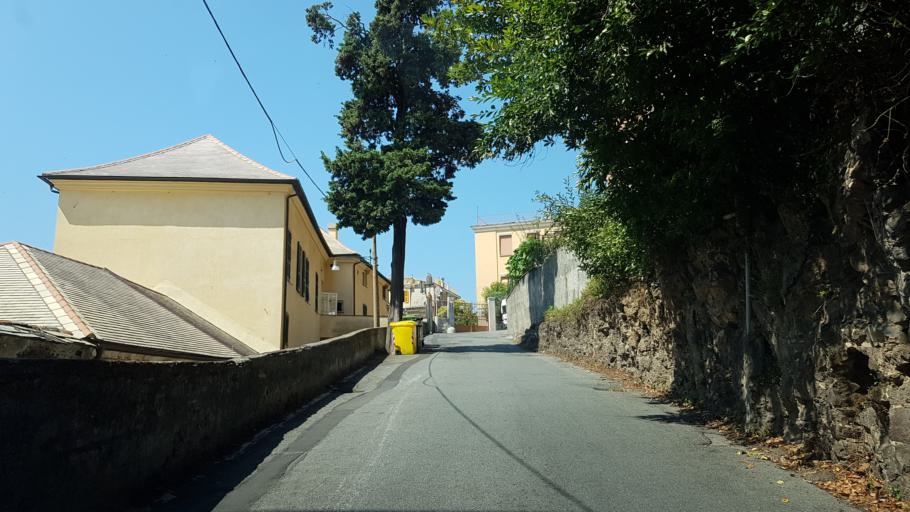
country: IT
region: Liguria
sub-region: Provincia di Genova
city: San Teodoro
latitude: 44.4171
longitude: 8.8682
